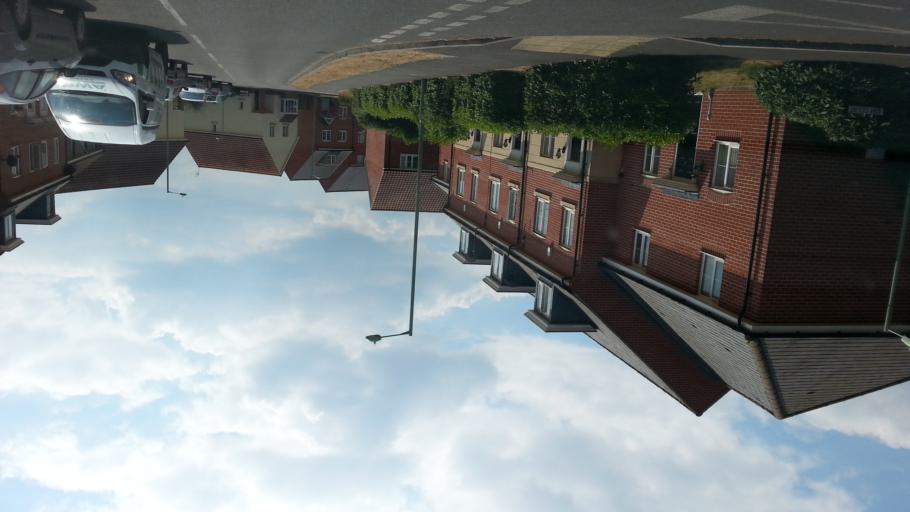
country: GB
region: England
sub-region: Cambridgeshire
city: Isleham
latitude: 52.3029
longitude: 0.4976
